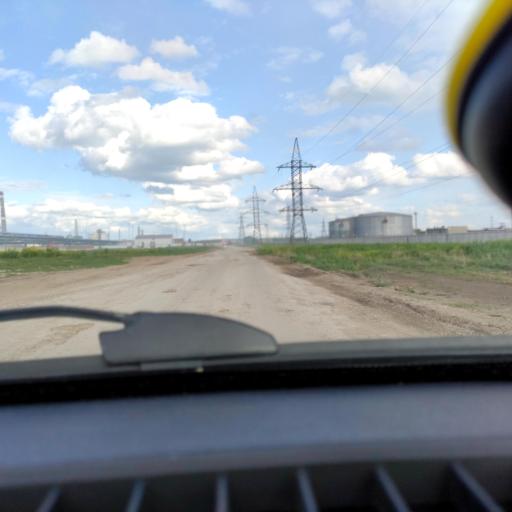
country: RU
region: Samara
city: Tol'yatti
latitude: 53.5482
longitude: 49.4652
